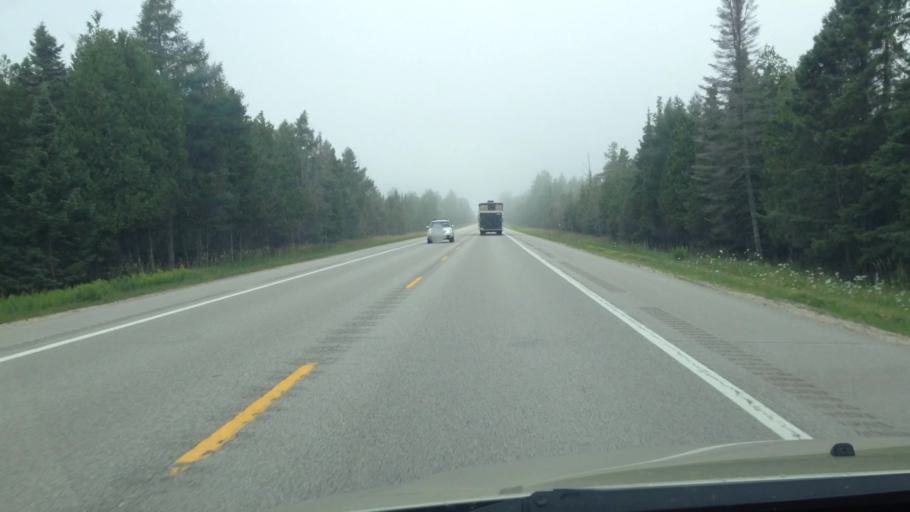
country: US
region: Michigan
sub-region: Luce County
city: Newberry
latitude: 46.1007
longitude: -85.5368
